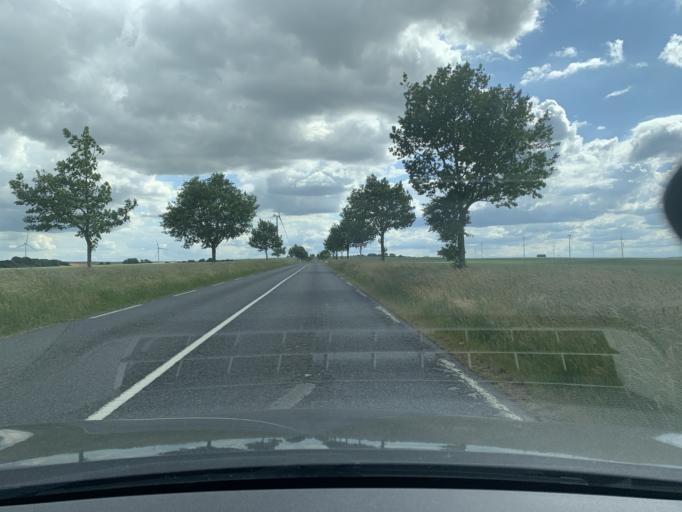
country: FR
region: Nord-Pas-de-Calais
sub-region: Departement du Pas-de-Calais
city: Hermies
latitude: 50.0290
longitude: 3.0392
